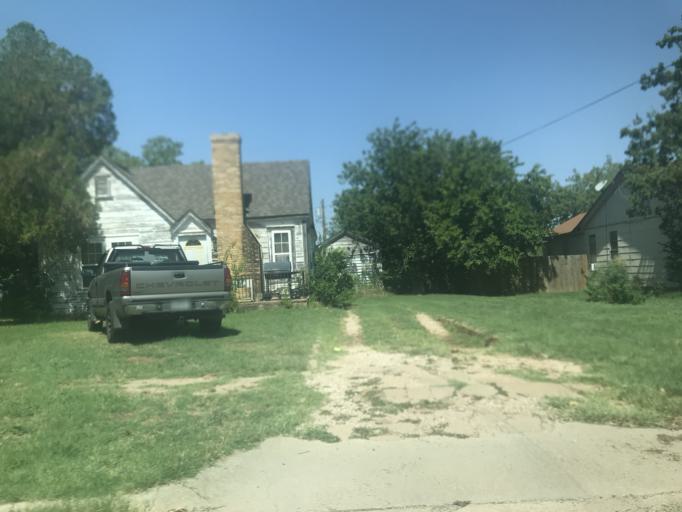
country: US
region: Texas
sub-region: Taylor County
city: Abilene
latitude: 32.4715
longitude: -99.7407
